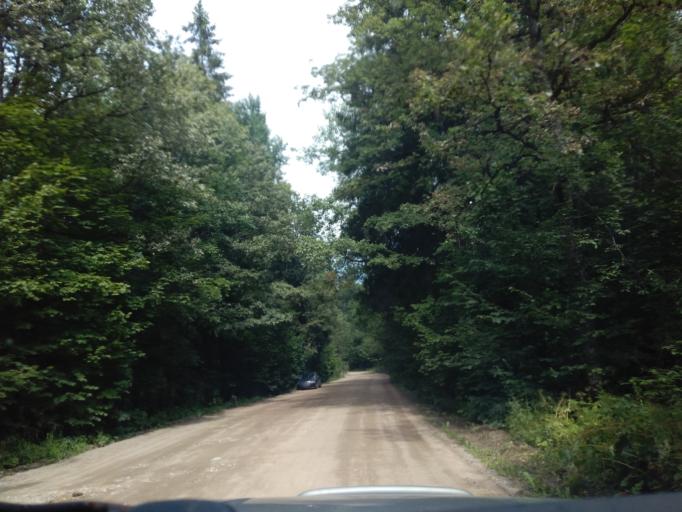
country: BY
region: Minsk
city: Khatsyezhyna
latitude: 53.9008
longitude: 27.2826
